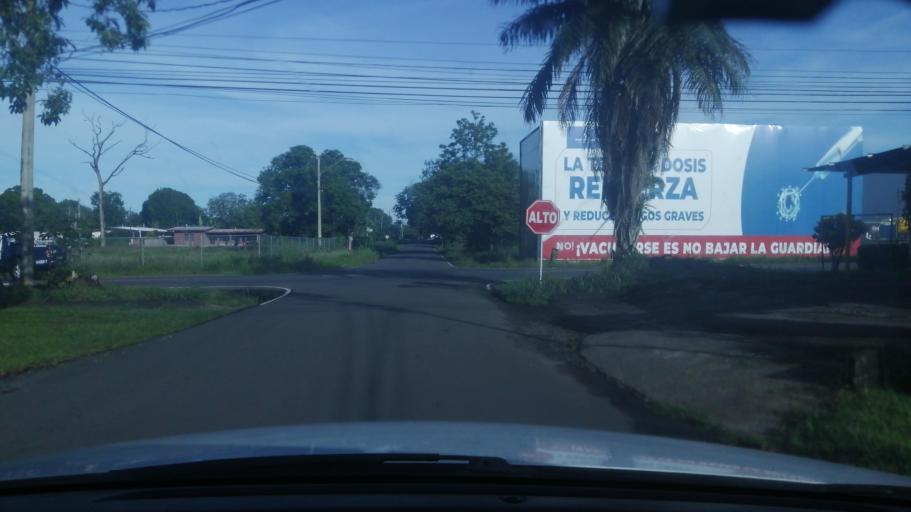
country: PA
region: Chiriqui
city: Mata del Nance
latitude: 8.4481
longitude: -82.4215
